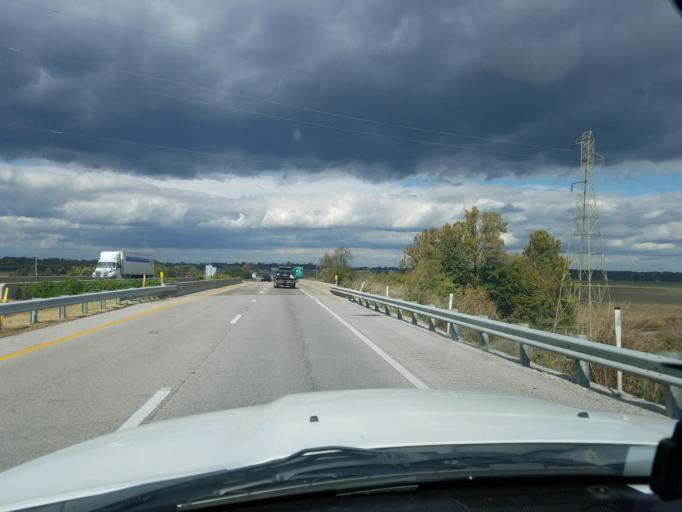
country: US
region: Kentucky
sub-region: Henderson County
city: Henderson
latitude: 37.8391
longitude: -87.5646
